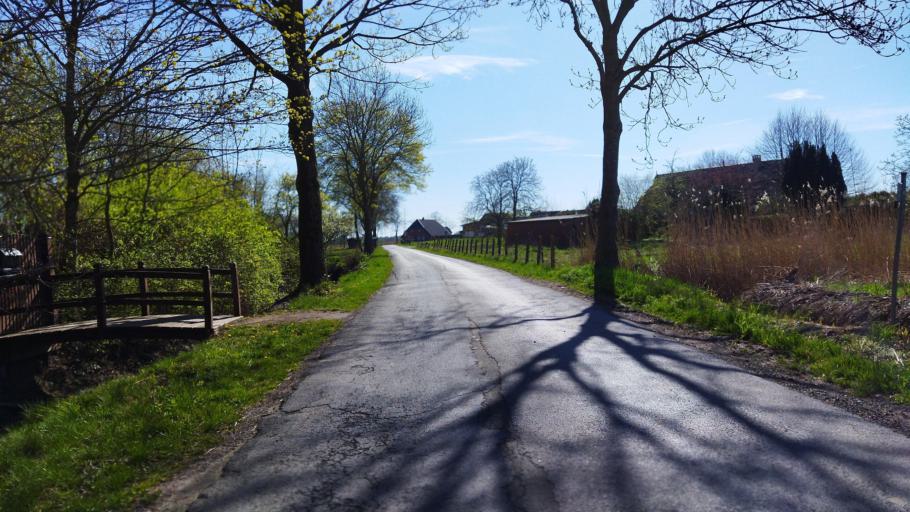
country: DE
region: Lower Saxony
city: Elsfleth
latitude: 53.2074
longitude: 8.4645
